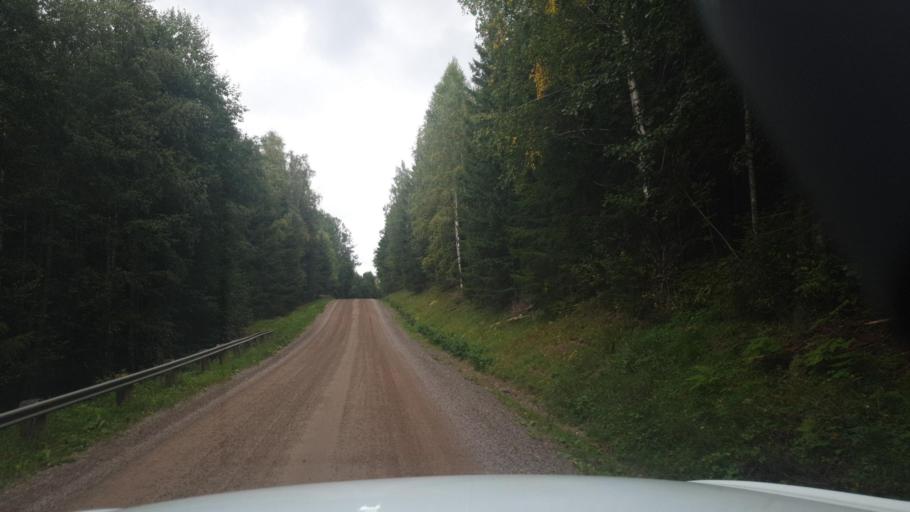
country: SE
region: Vaermland
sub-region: Arvika Kommun
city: Arvika
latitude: 60.0130
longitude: 12.6464
